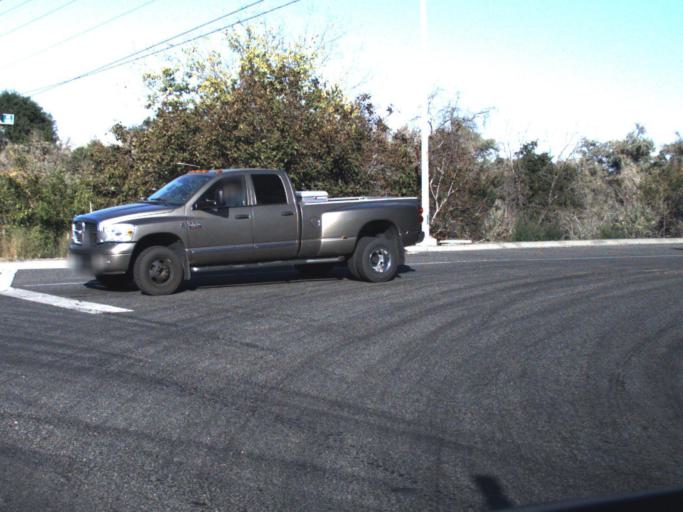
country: US
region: Washington
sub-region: Benton County
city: Richland
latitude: 46.2931
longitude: -119.3062
